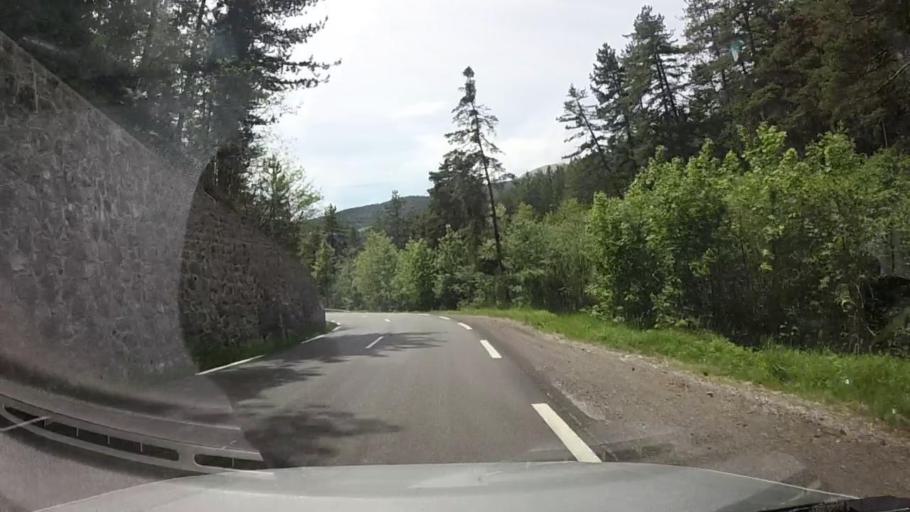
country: FR
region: Provence-Alpes-Cote d'Azur
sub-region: Departement des Alpes-de-Haute-Provence
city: Le Brusquet
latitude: 44.2397
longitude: 6.3626
